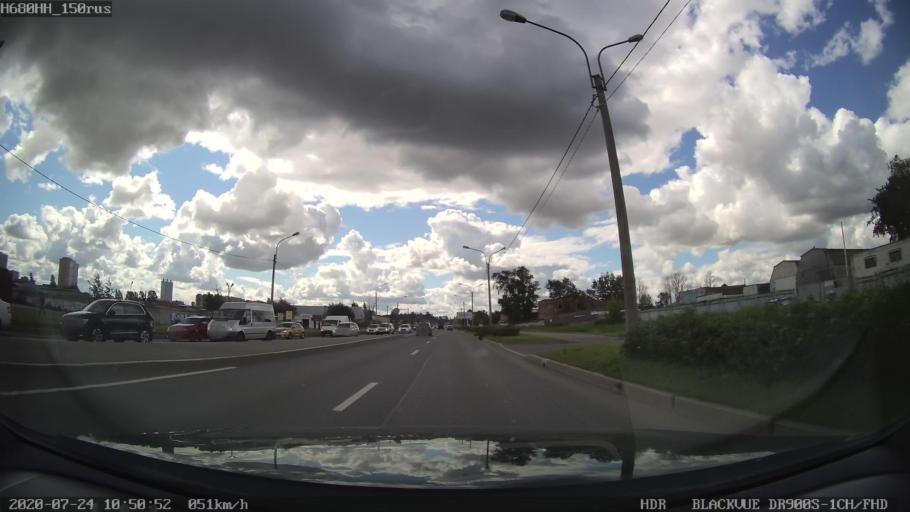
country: RU
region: St.-Petersburg
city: Admiralteisky
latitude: 59.8957
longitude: 30.3003
